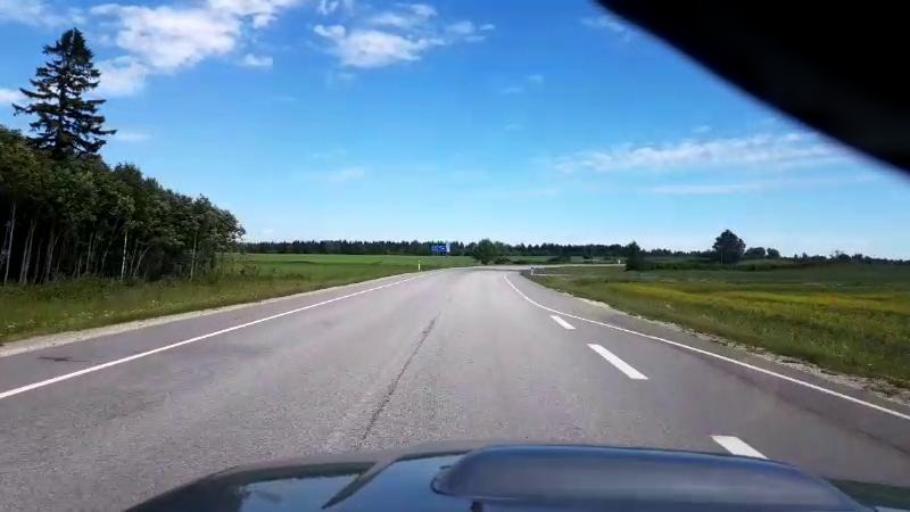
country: EE
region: Jaervamaa
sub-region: Koeru vald
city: Koeru
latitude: 58.9888
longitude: 25.9829
